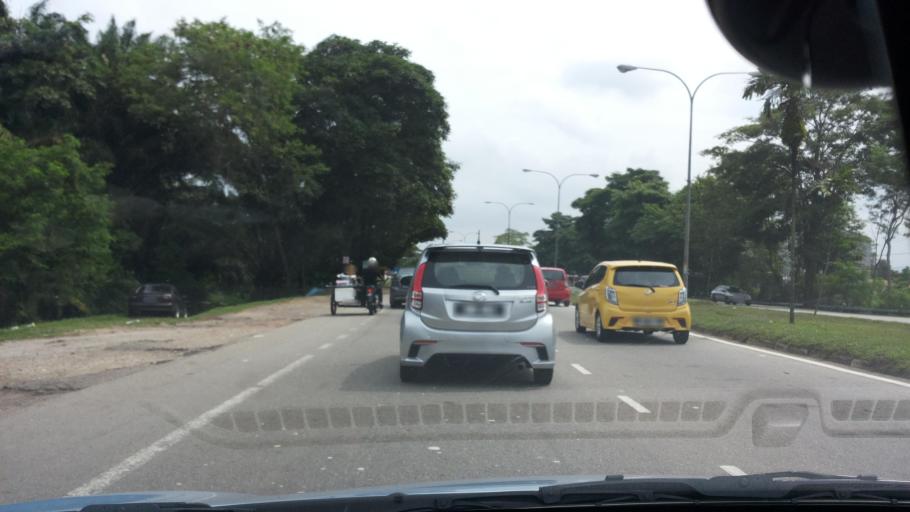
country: MY
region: Pahang
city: Kuantan
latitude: 3.7673
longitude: 103.2226
